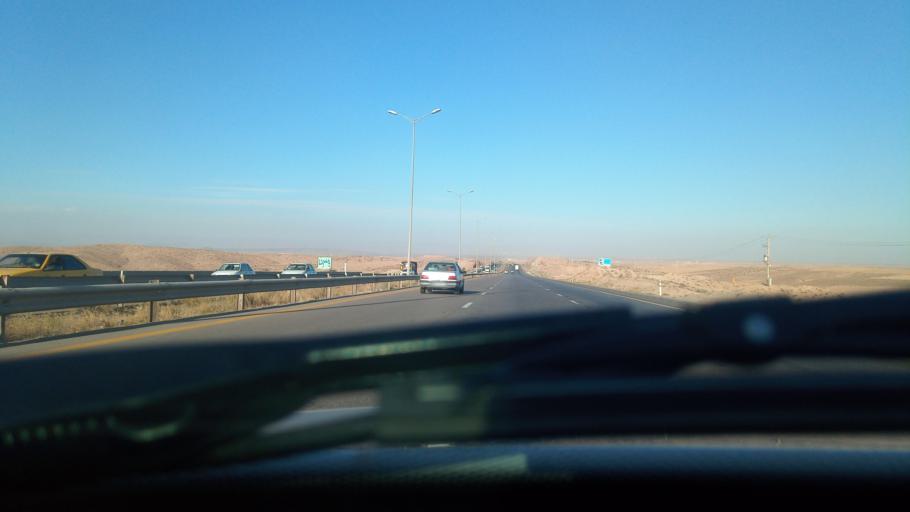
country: IR
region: Razavi Khorasan
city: Mashhad
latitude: 36.0488
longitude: 59.7051
